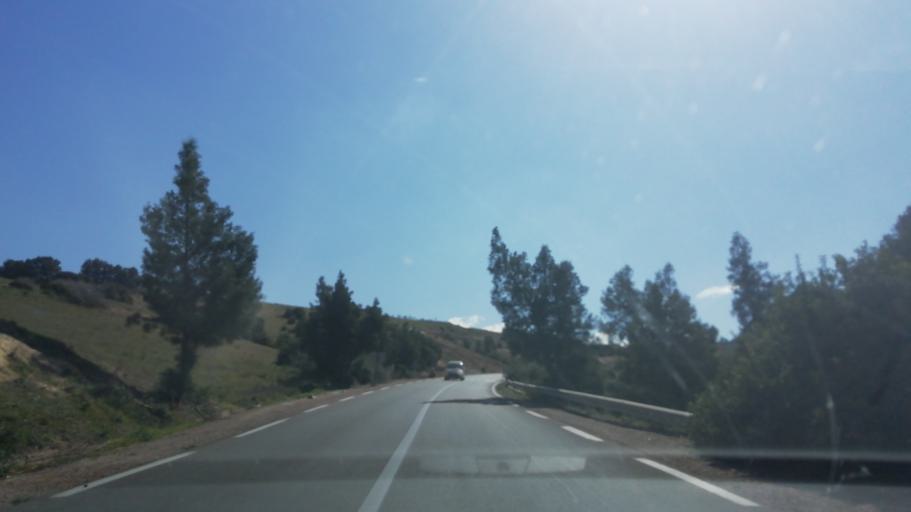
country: DZ
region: Mascara
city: Mascara
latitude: 35.4959
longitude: 0.1333
